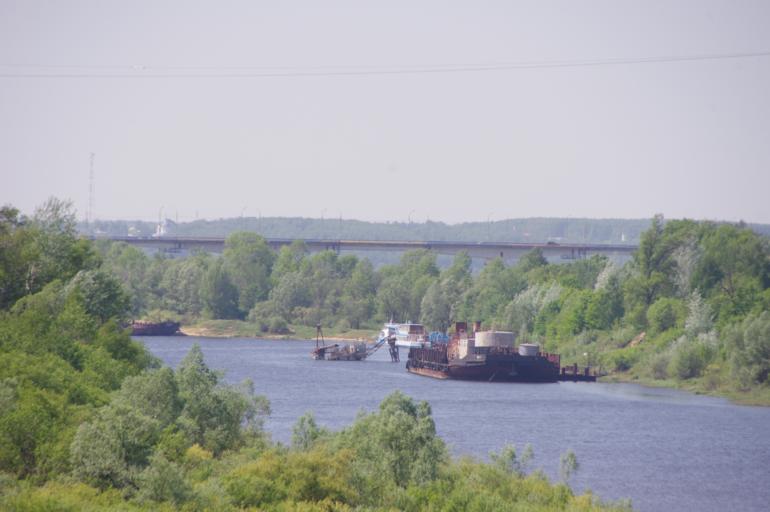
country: RU
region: Rjazan
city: Kasimov
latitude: 54.9413
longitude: 41.3715
